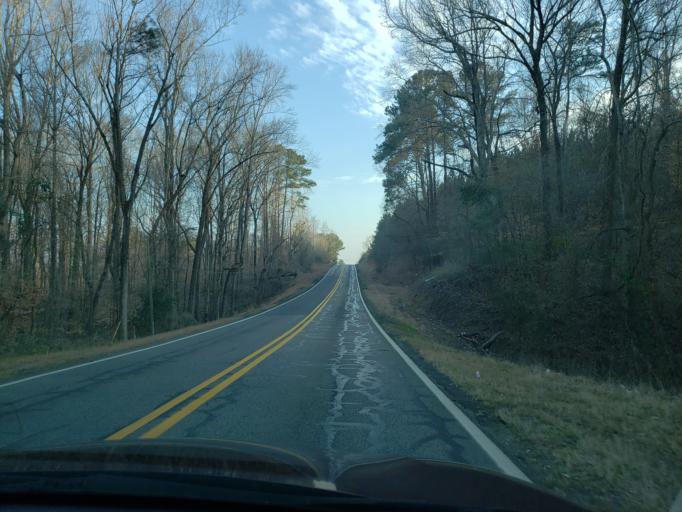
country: US
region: Alabama
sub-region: Hale County
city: Greensboro
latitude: 32.8092
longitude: -87.5947
